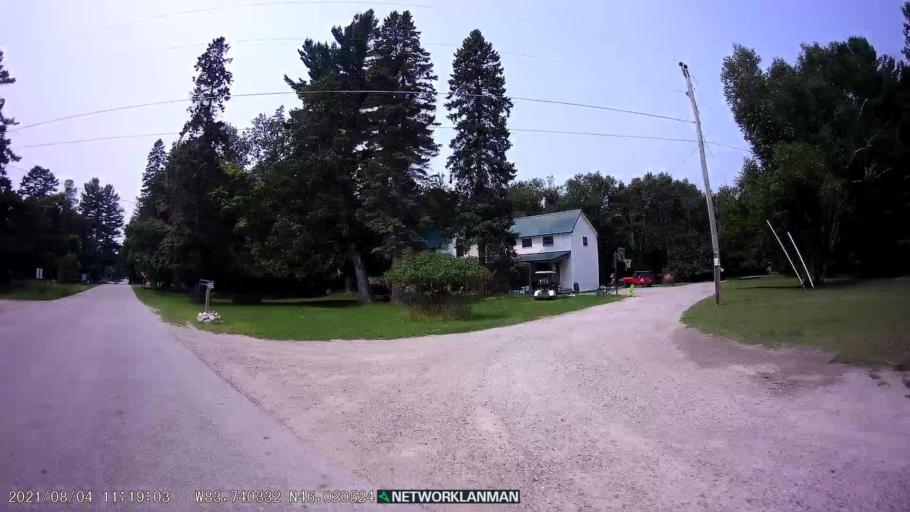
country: CA
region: Ontario
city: Thessalon
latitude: 46.0205
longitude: -83.7403
